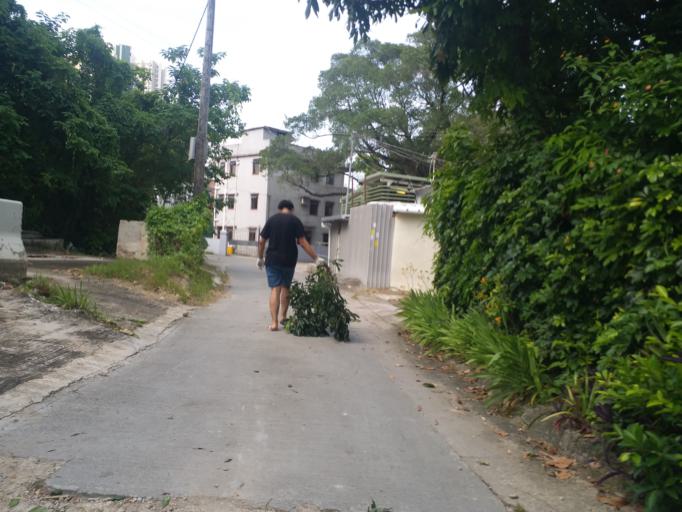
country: HK
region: Yuen Long
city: Yuen Long Kau Hui
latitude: 22.4421
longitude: 114.0033
